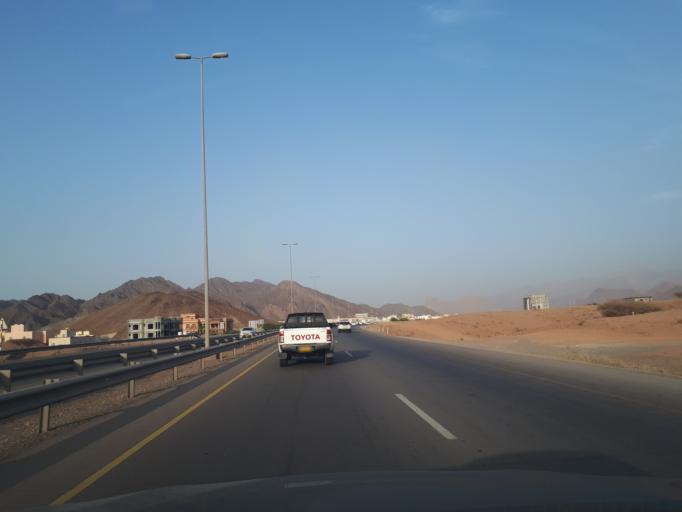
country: OM
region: Muhafazat ad Dakhiliyah
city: Bidbid
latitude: 23.4673
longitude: 58.1375
